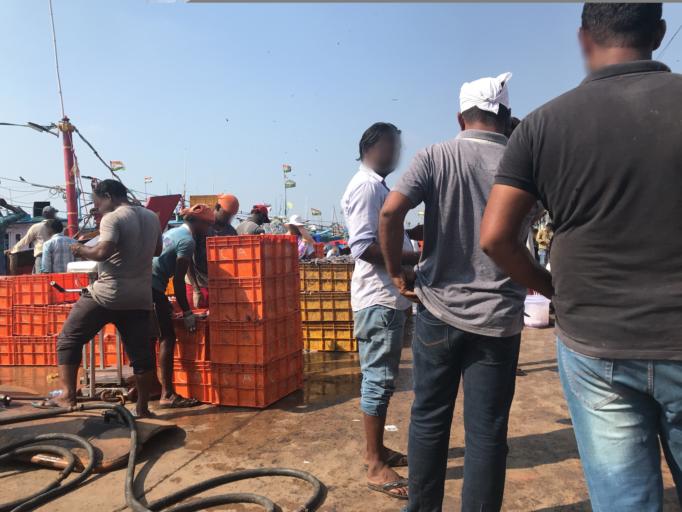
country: IN
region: Karnataka
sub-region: Dakshina Kannada
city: Ullal
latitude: 12.8538
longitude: 74.8333
